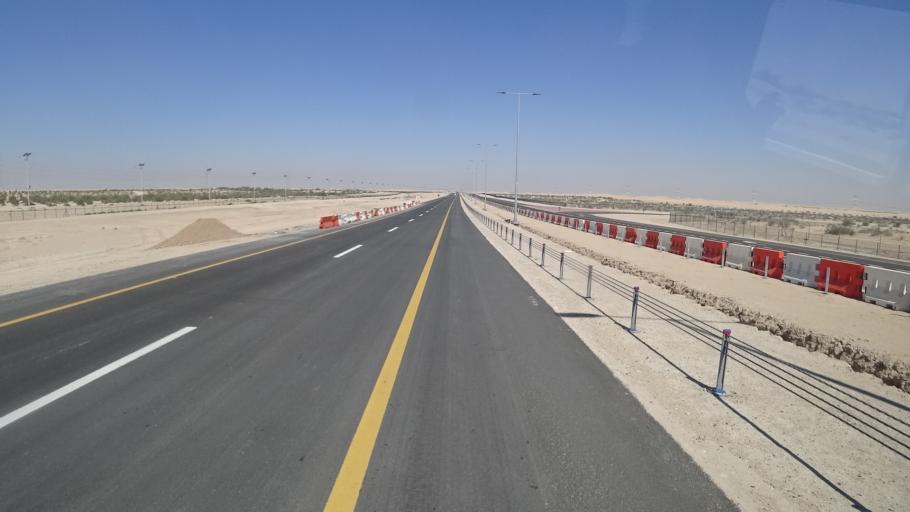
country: AE
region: Abu Dhabi
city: Abu Dhabi
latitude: 24.1383
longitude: 54.8408
